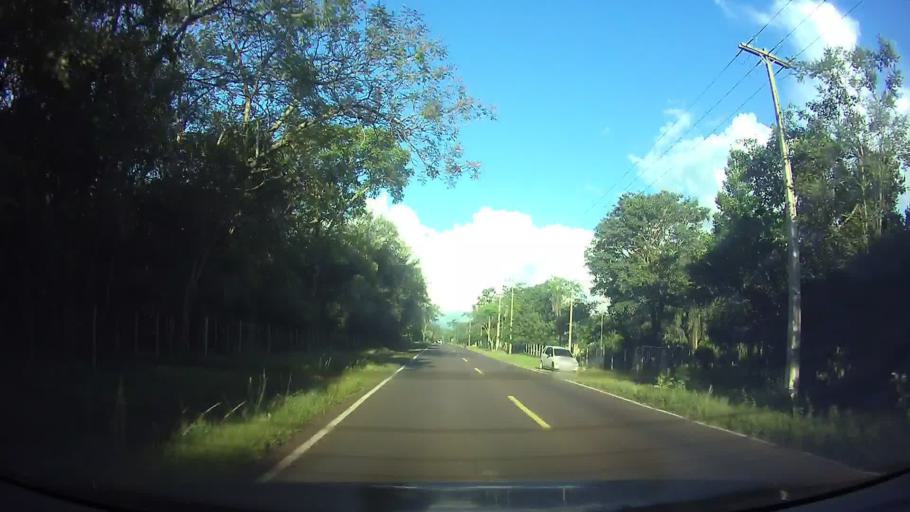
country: PY
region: Cordillera
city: Emboscada
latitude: -25.2038
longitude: -57.3401
